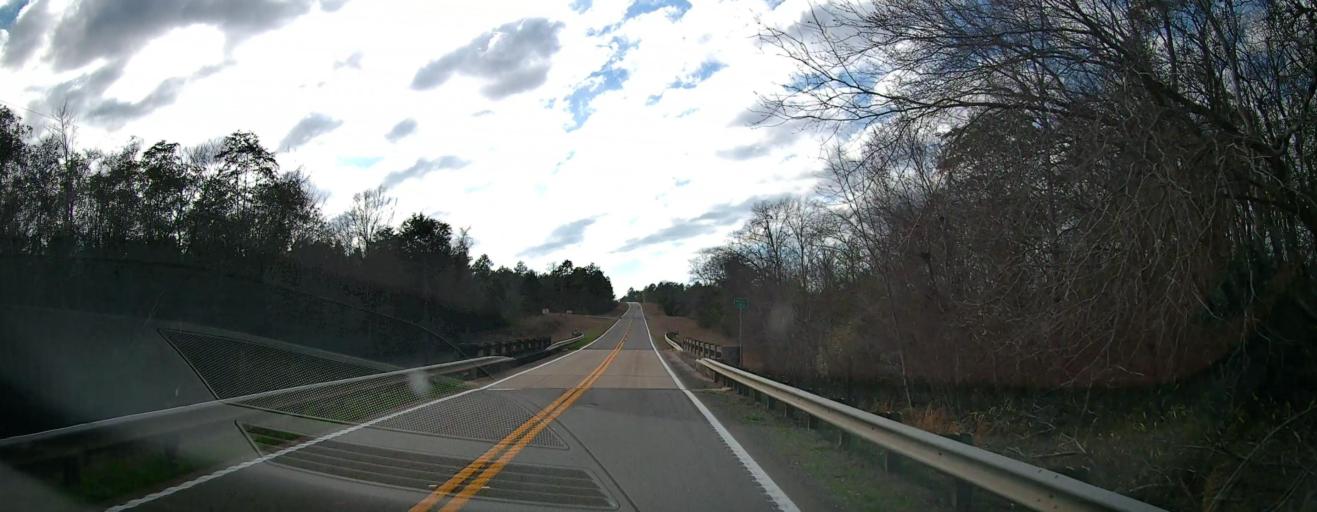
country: US
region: Georgia
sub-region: Marion County
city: Buena Vista
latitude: 32.4407
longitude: -84.4883
